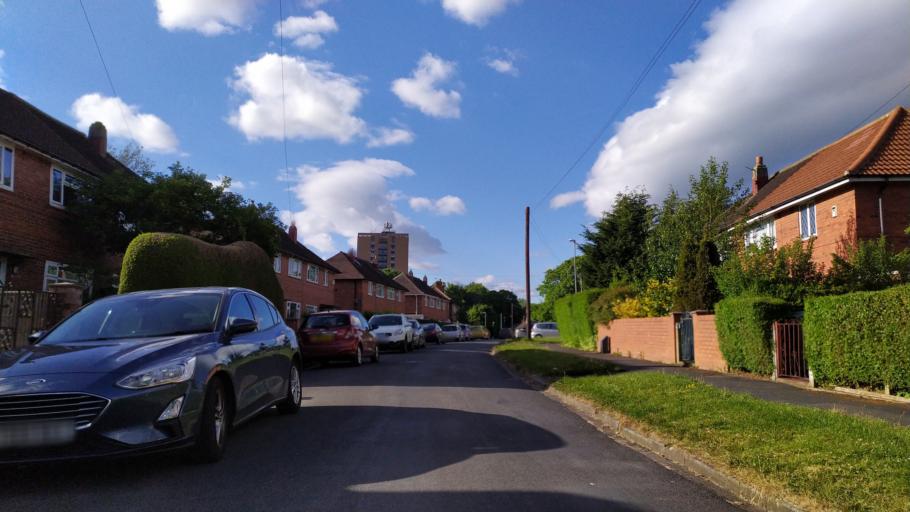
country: GB
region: England
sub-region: City and Borough of Leeds
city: Chapel Allerton
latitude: 53.8228
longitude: -1.5407
